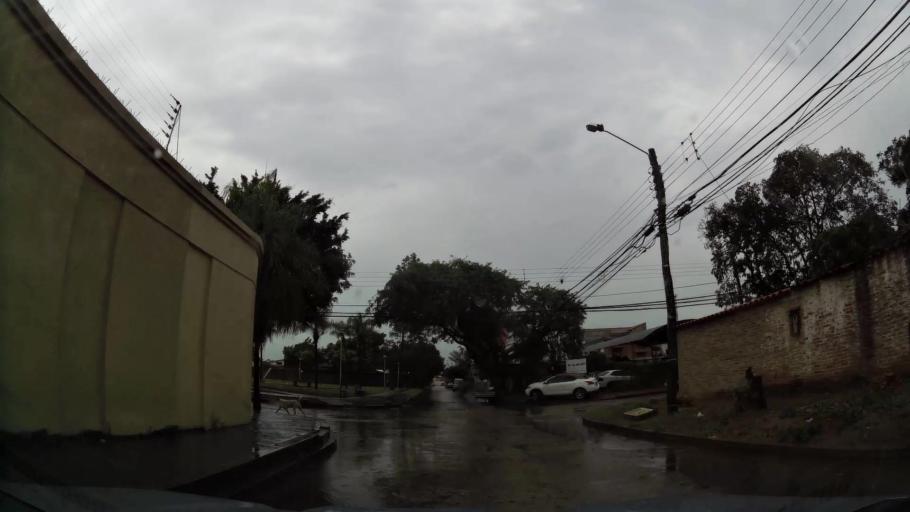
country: BO
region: Santa Cruz
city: Santa Cruz de la Sierra
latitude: -17.7928
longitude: -63.2086
